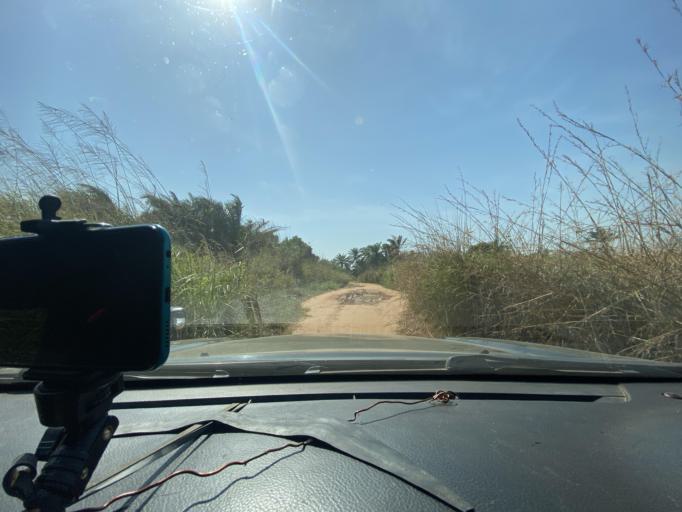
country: CD
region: Kasai-Oriental
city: Kabinda
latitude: -6.0979
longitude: 24.5458
